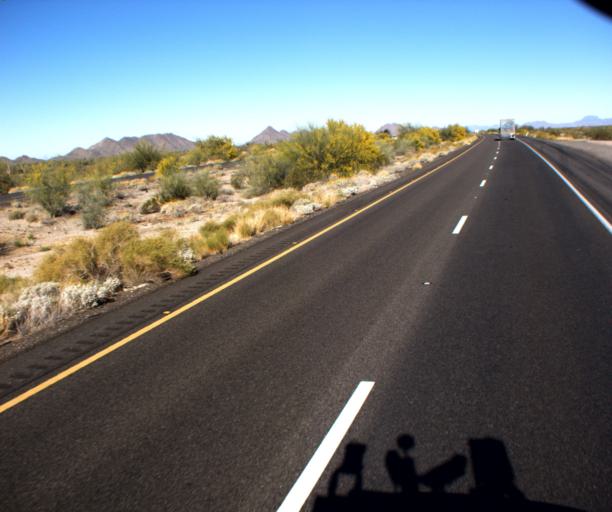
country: US
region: Arizona
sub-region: Maricopa County
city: Gila Bend
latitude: 32.8769
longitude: -112.4485
